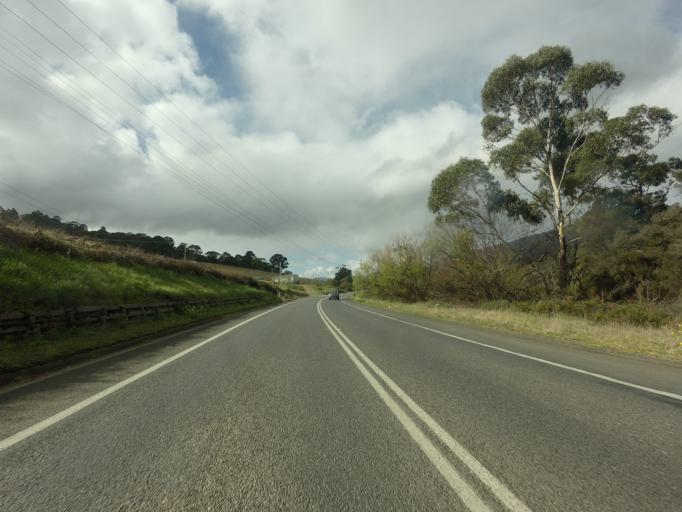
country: AU
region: Tasmania
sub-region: Huon Valley
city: Huonville
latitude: -43.0573
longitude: 147.0304
